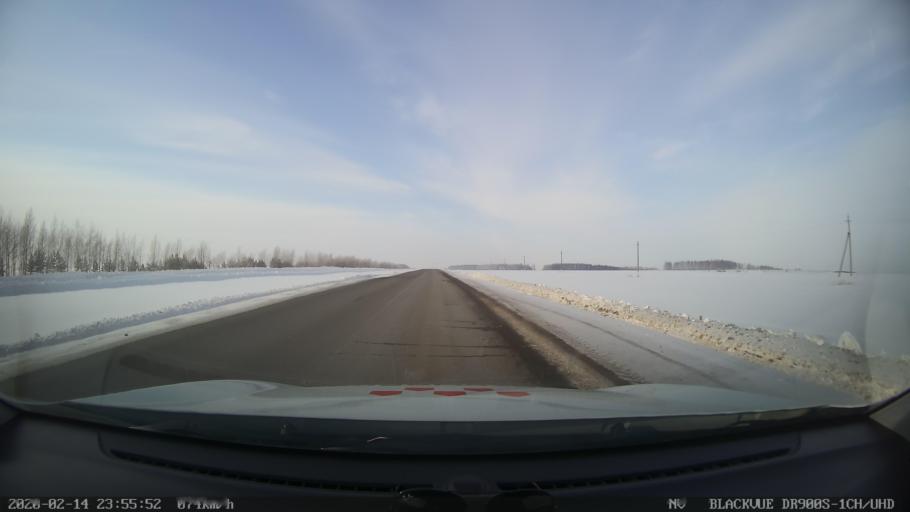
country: RU
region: Tatarstan
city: Kuybyshevskiy Zaton
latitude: 55.3192
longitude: 49.1392
